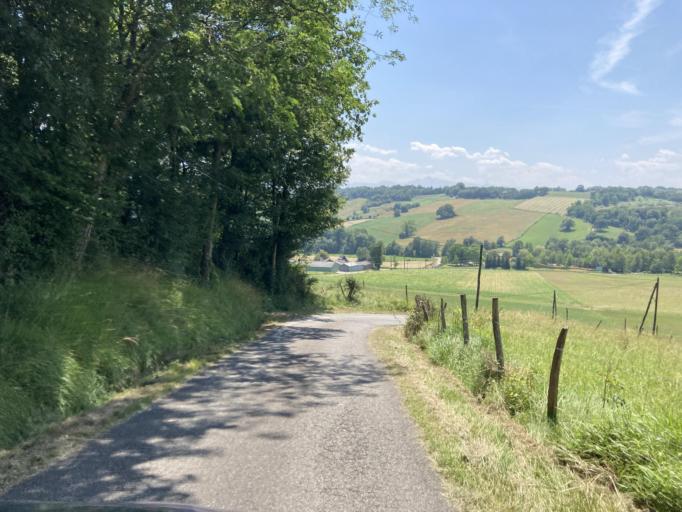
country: FR
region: Aquitaine
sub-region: Departement des Pyrenees-Atlantiques
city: Ledeuix
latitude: 43.2298
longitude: -0.5653
